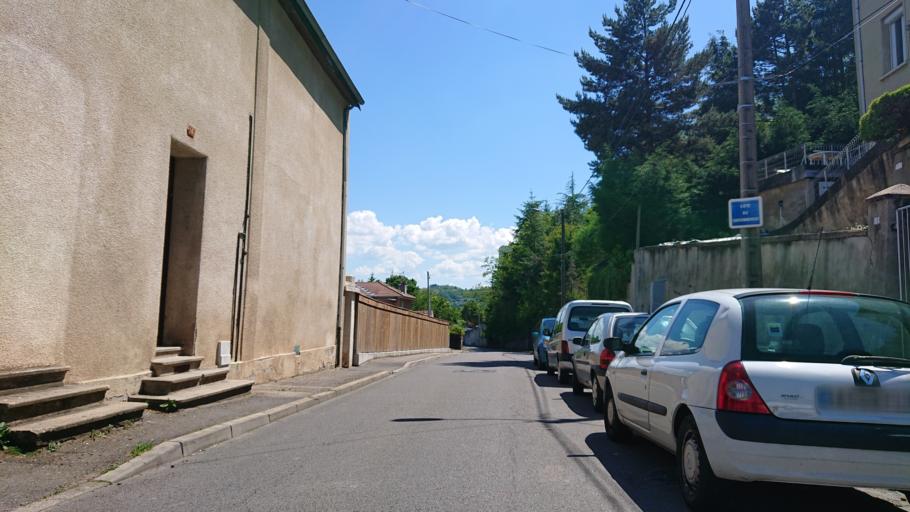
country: FR
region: Rhone-Alpes
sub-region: Departement de la Loire
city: Villars
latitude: 45.4496
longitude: 4.3605
